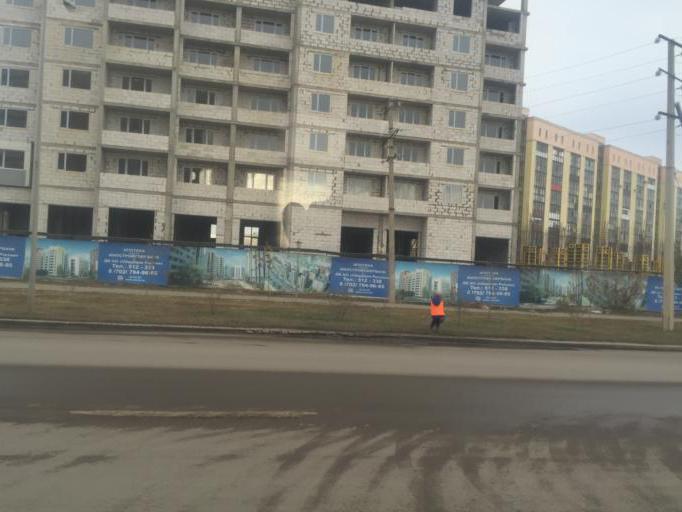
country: KZ
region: Astana Qalasy
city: Astana
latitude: 51.1680
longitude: 71.3927
